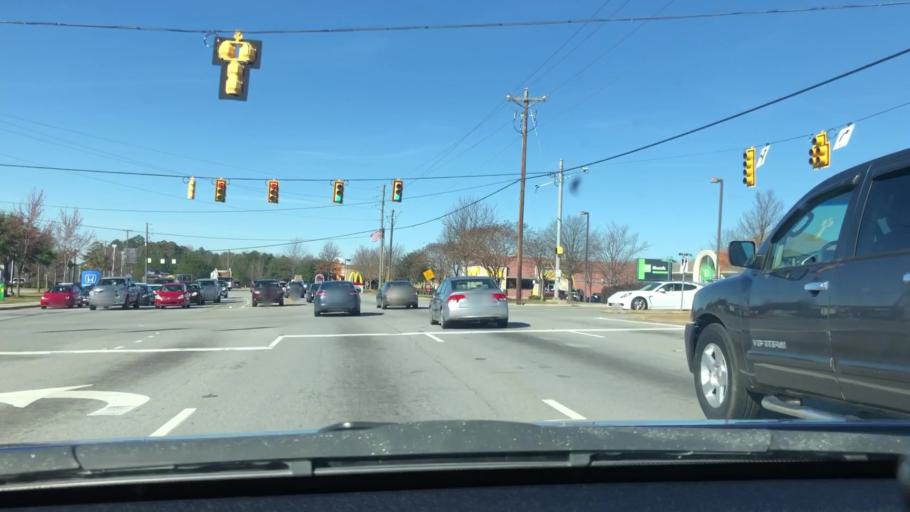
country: US
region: South Carolina
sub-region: Lexington County
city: Oak Grove
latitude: 34.0138
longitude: -81.1523
